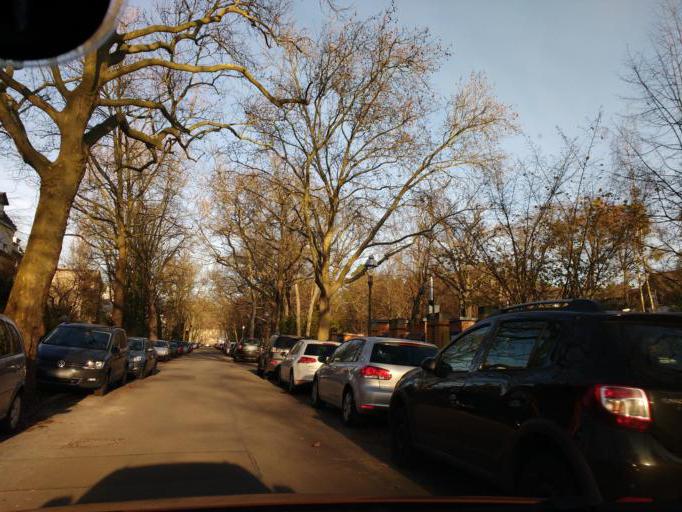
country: DE
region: Berlin
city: Nikolassee
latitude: 52.4301
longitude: 13.2176
